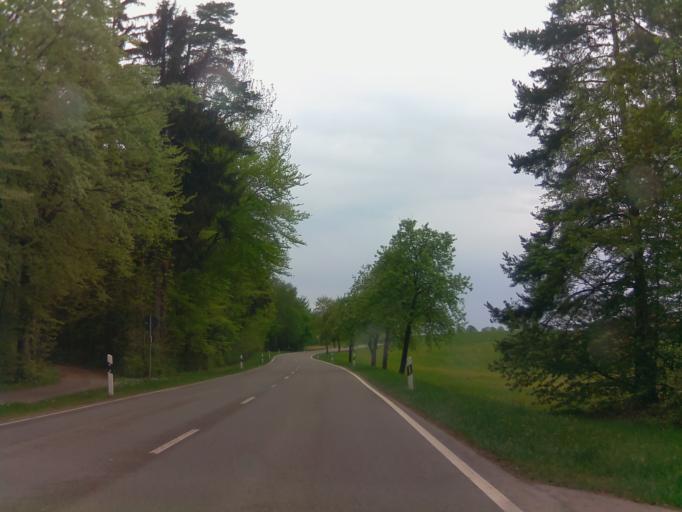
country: DE
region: Baden-Wuerttemberg
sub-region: Freiburg Region
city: Zimmern ob Rottweil
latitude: 48.1648
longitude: 8.5846
